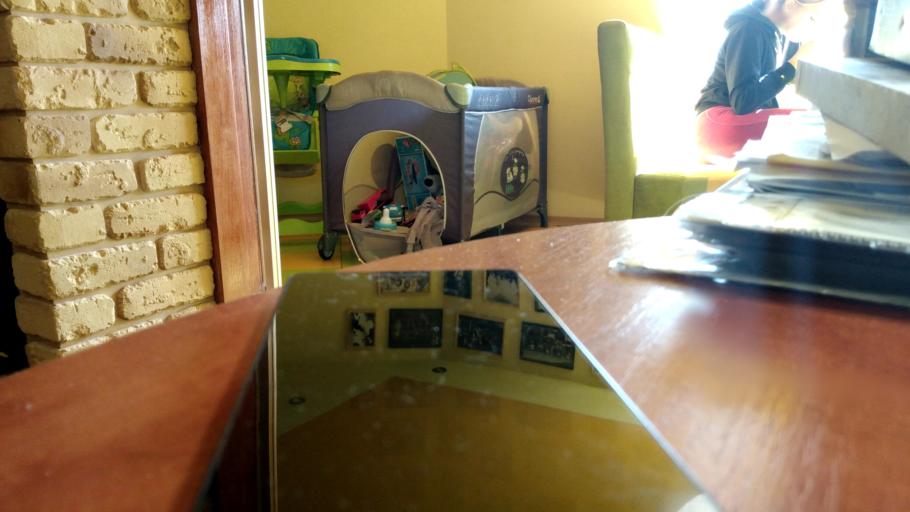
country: RU
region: Penza
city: Serdobsk
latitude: 52.4124
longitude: 44.3189
